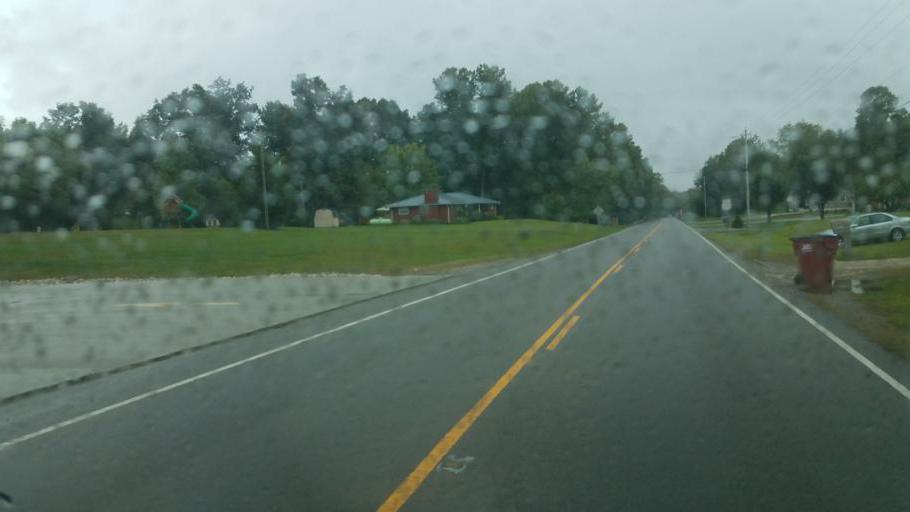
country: US
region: Ohio
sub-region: Scioto County
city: Wheelersburg
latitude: 38.7643
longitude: -82.8097
